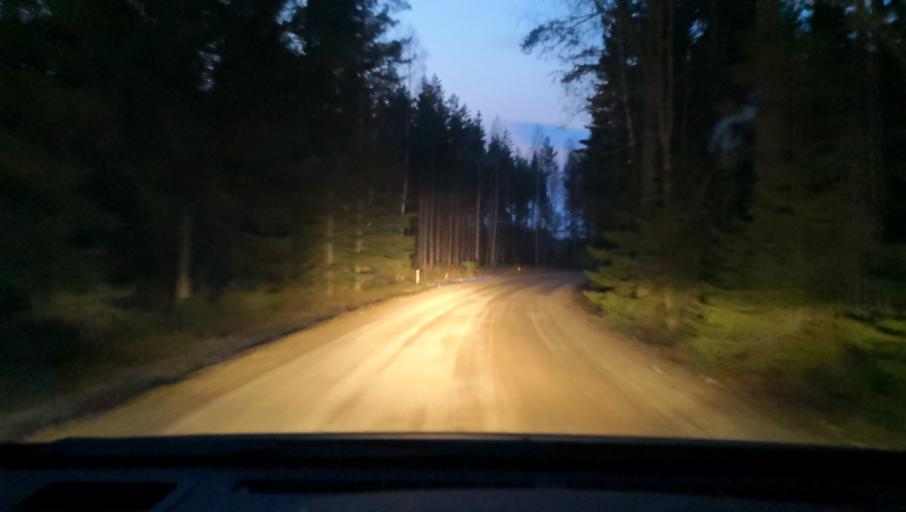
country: SE
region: OErebro
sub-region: Lindesbergs Kommun
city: Frovi
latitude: 59.5901
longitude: 15.4702
